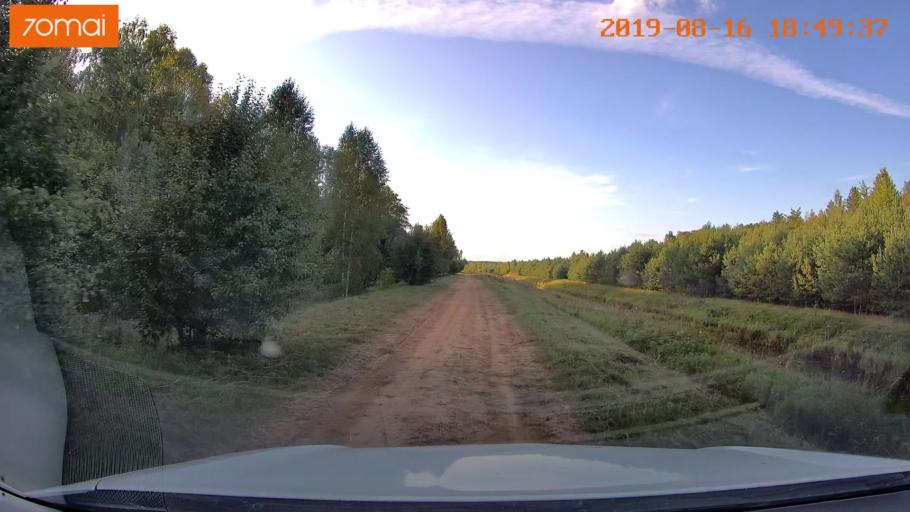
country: BY
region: Mogilev
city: Asipovichy
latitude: 53.2378
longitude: 28.6652
